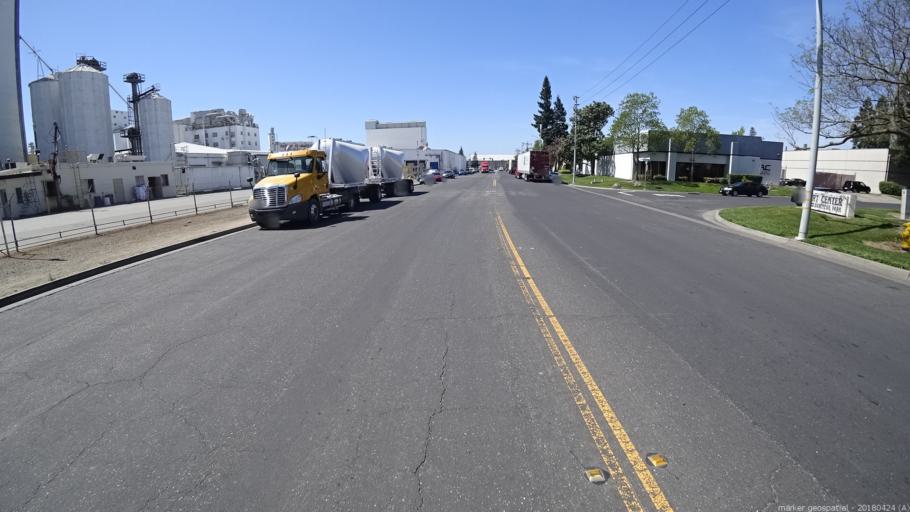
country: US
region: California
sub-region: Yolo County
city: West Sacramento
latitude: 38.5668
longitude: -121.5416
